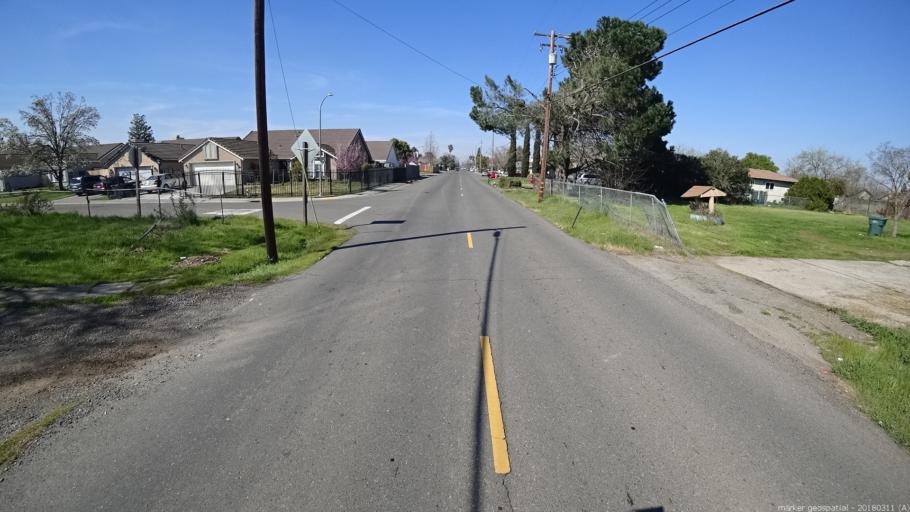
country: US
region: California
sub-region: Sacramento County
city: Florin
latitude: 38.4652
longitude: -121.3928
